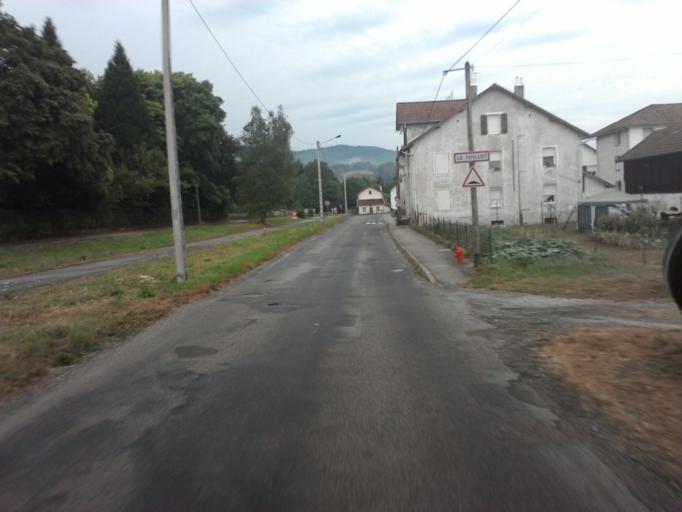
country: FR
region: Lorraine
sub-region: Departement des Vosges
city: Le Thillot
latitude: 47.8754
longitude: 6.7711
